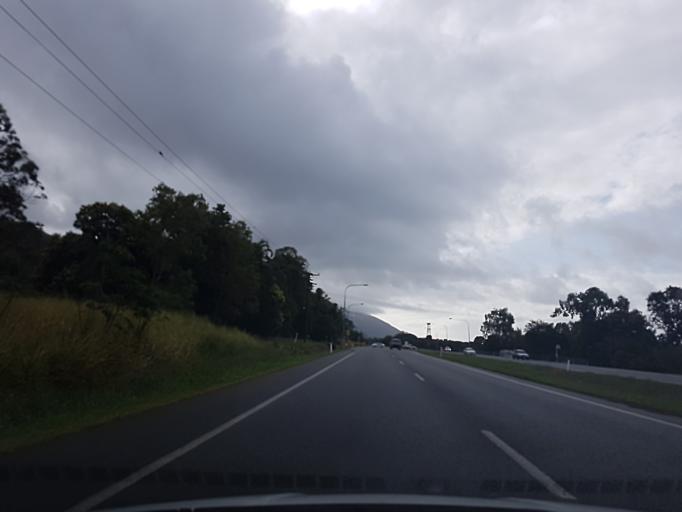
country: AU
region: Queensland
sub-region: Cairns
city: Trinity Beach
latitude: -16.8065
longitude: 145.6910
